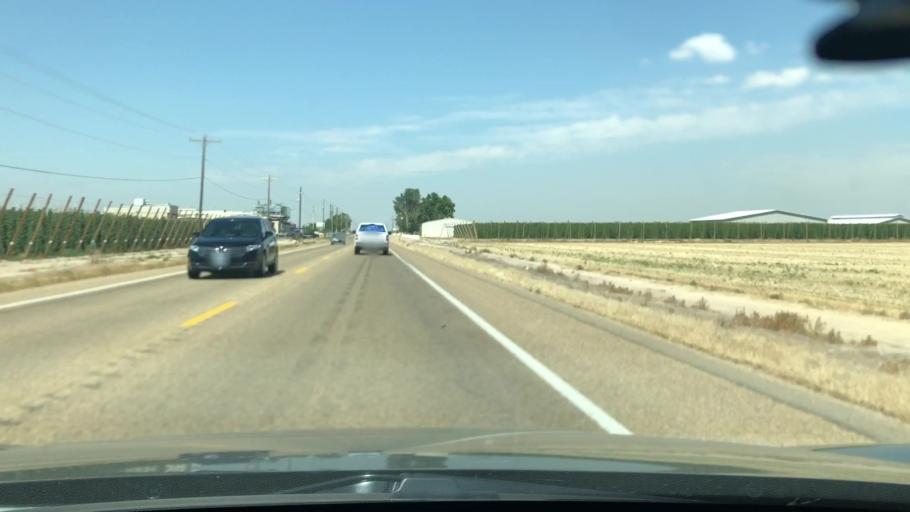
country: US
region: Idaho
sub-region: Canyon County
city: Wilder
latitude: 43.6922
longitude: -116.9120
